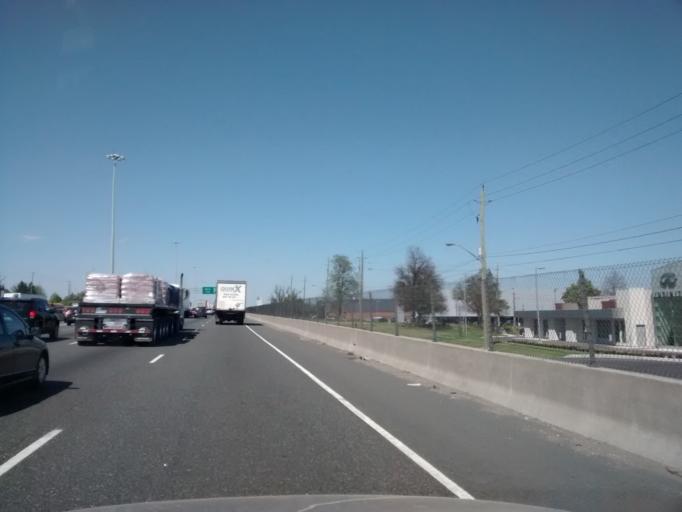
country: CA
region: Ontario
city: Oakville
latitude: 43.4160
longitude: -79.7337
